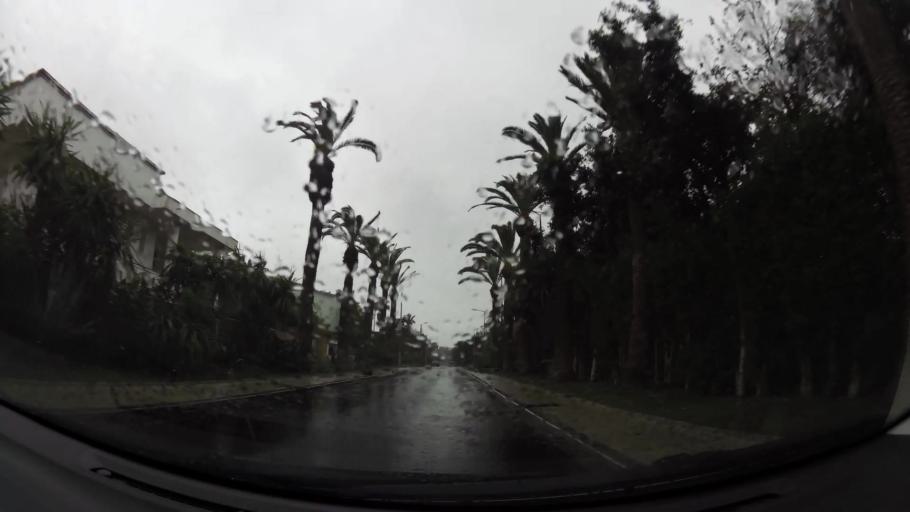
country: MA
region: Grand Casablanca
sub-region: Casablanca
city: Casablanca
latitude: 33.5853
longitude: -7.6657
